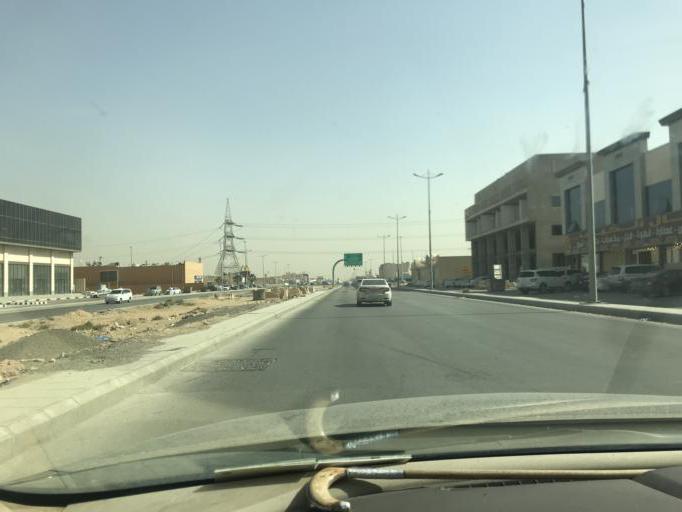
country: SA
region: Ar Riyad
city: Riyadh
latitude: 24.8192
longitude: 46.7305
